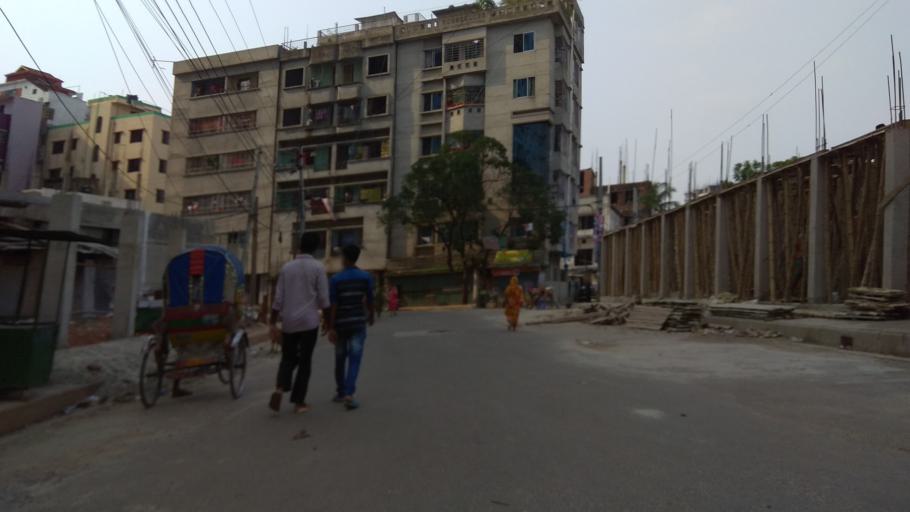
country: BD
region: Dhaka
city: Azimpur
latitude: 23.8132
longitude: 90.3598
